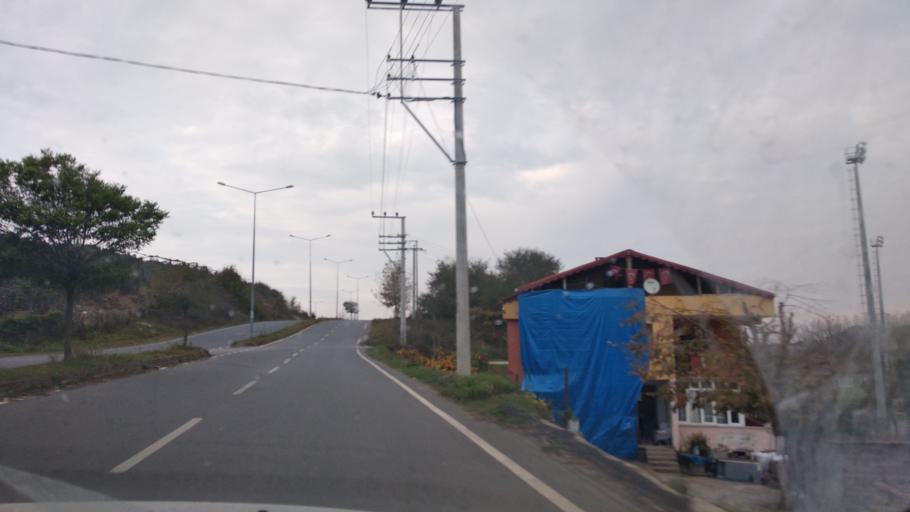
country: TR
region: Sakarya
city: Ortakoy
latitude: 41.0433
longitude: 30.6395
